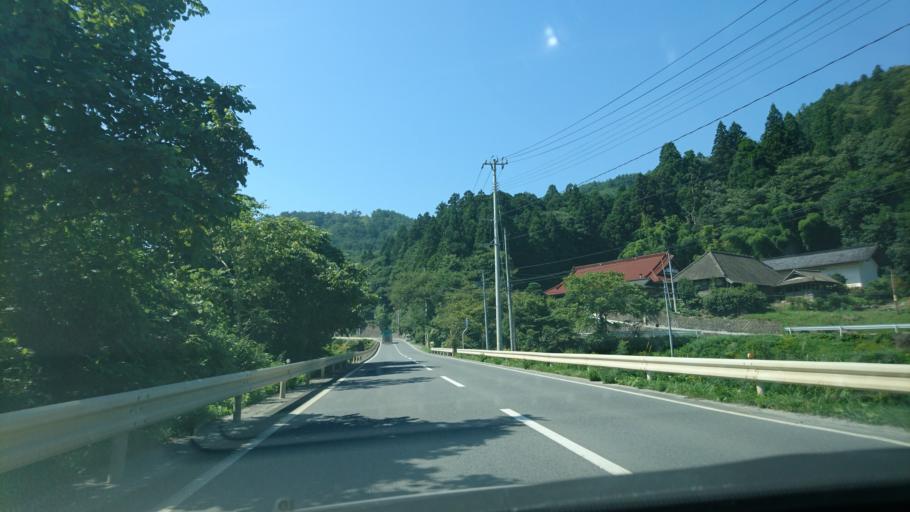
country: JP
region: Iwate
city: Ofunato
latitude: 39.0234
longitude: 141.5716
